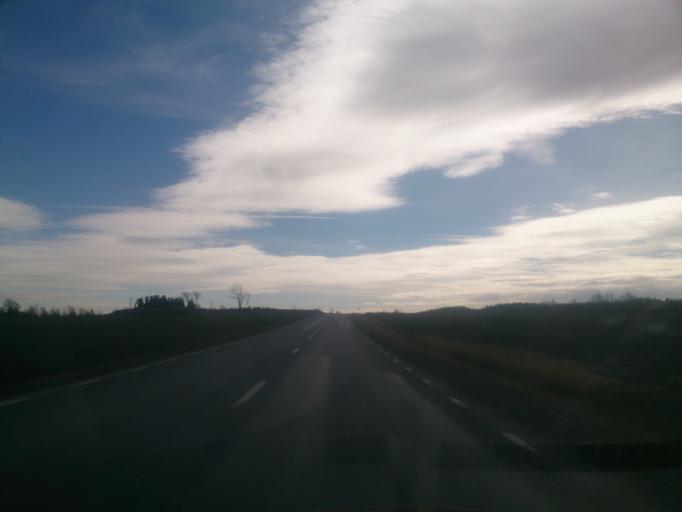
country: SE
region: OEstergoetland
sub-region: Norrkopings Kommun
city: Skarblacka
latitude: 58.6030
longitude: 15.8269
